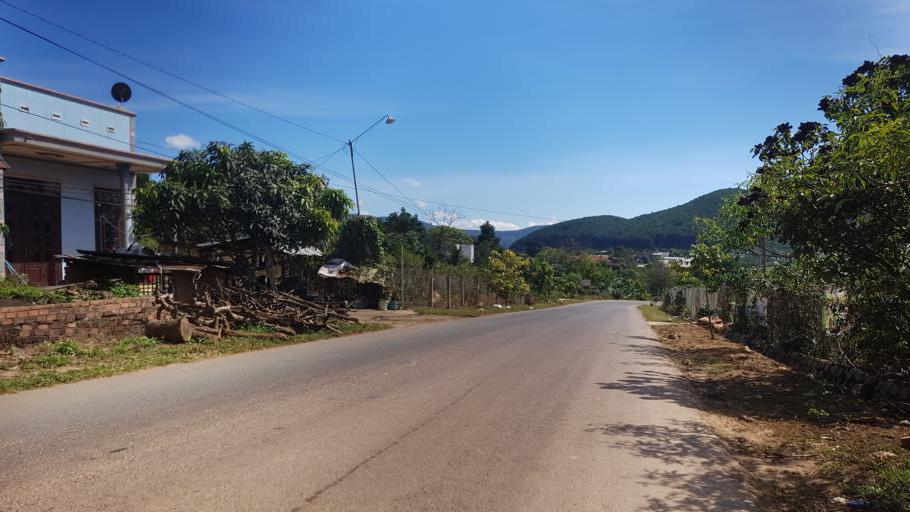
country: VN
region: Lam Dong
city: Da Lat
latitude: 11.8783
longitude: 108.3424
